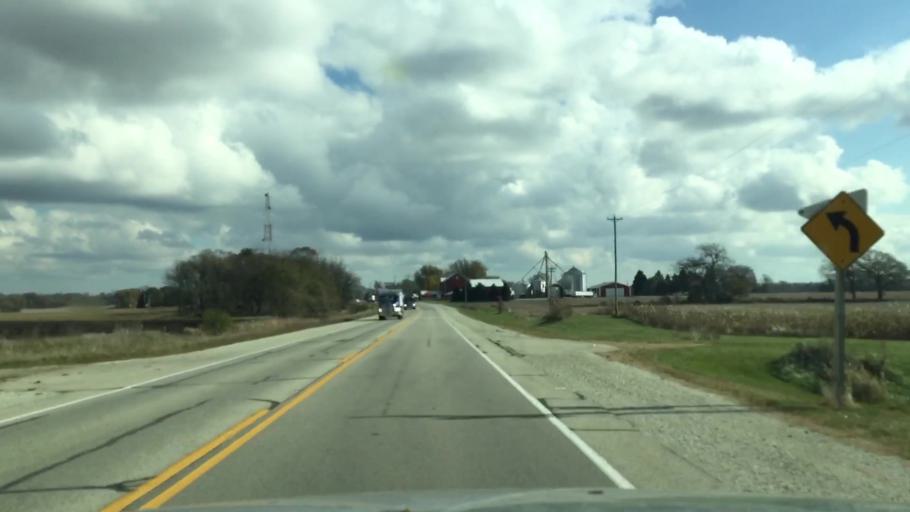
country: US
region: Wisconsin
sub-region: Racine County
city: Eagle Lake
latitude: 42.7414
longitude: -88.1194
